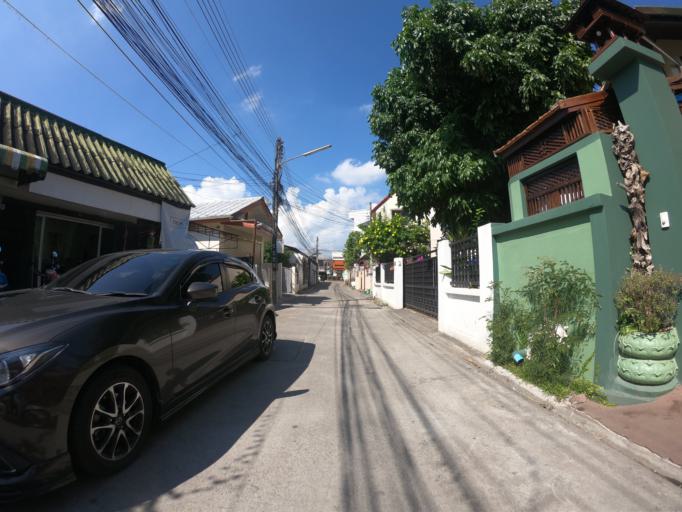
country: TH
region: Chiang Mai
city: Chiang Mai
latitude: 18.7779
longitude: 98.9851
